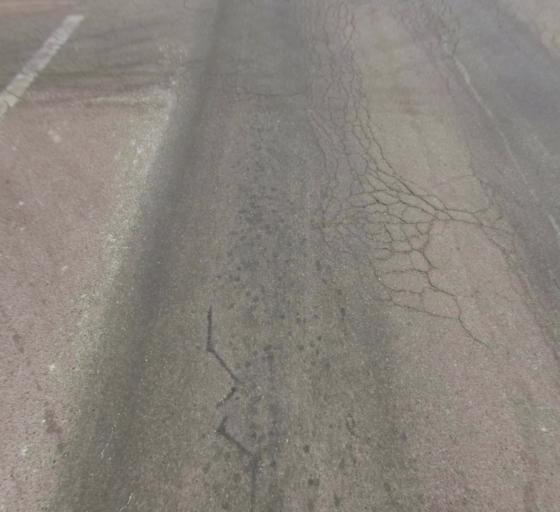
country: US
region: California
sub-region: Madera County
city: Parkwood
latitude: 36.8480
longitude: -120.1334
